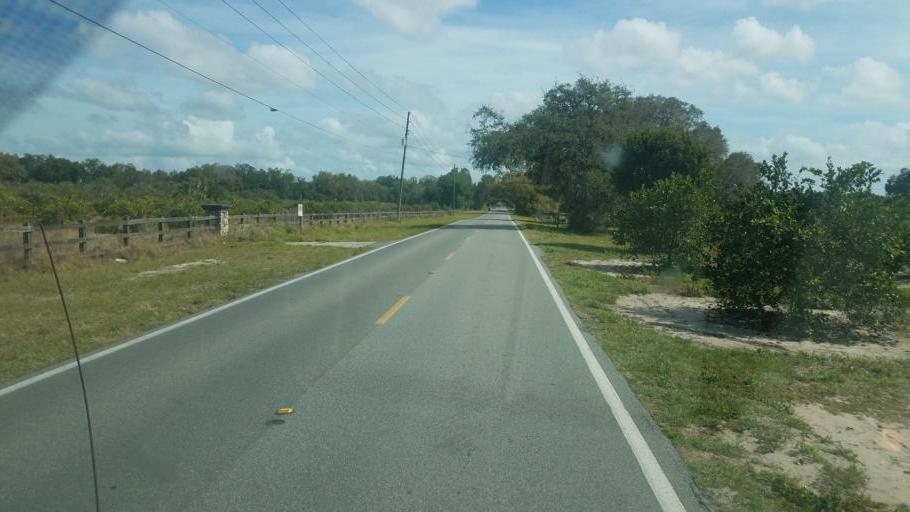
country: US
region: Florida
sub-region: Polk County
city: Lake Wales
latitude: 27.9250
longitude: -81.5337
